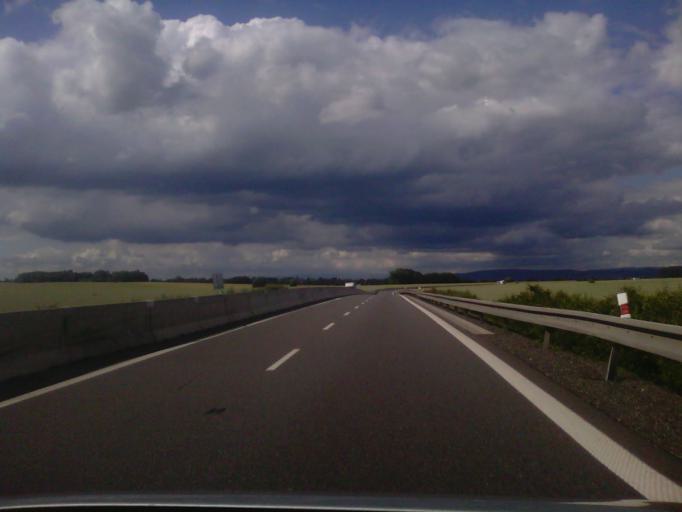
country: CZ
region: Olomoucky
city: Hnevotin
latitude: 49.5968
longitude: 17.1986
